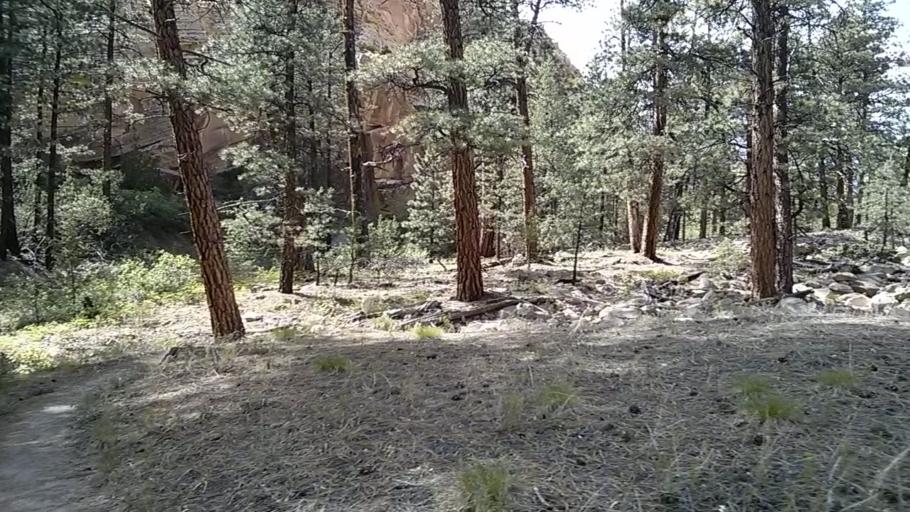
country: US
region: Utah
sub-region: Wayne County
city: Loa
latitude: 37.8816
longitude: -111.6331
